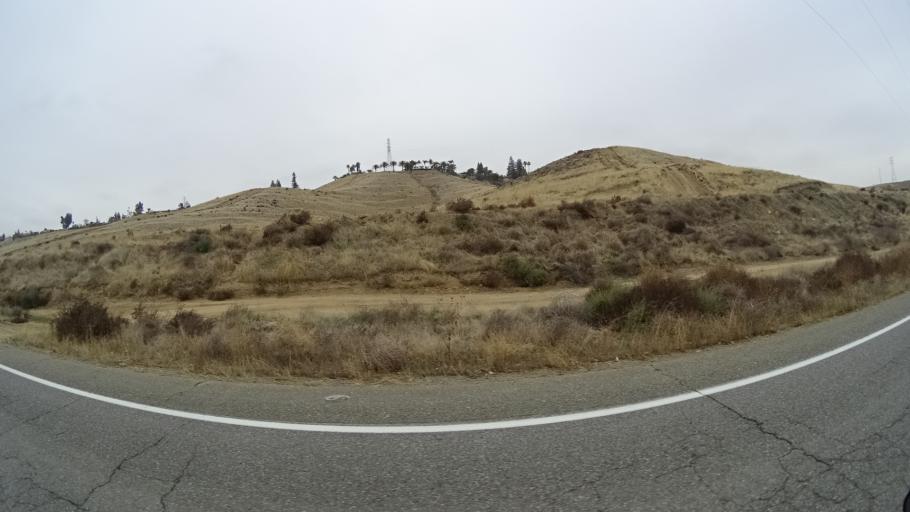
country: US
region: California
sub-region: Kern County
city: Oildale
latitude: 35.4134
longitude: -118.9370
